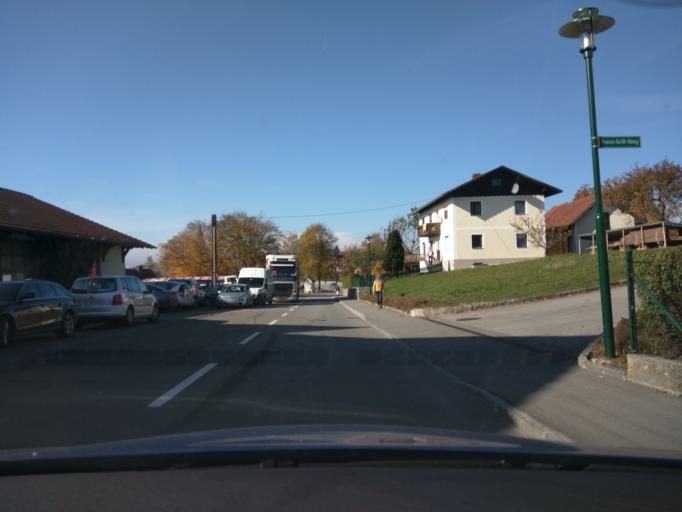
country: DE
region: Bavaria
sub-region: Lower Bavaria
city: Obernzell
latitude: 48.5428
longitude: 13.5773
